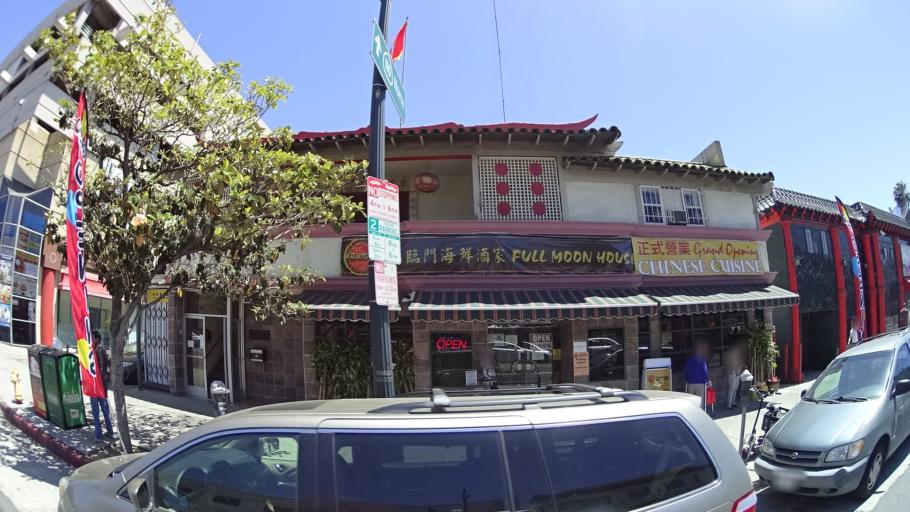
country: US
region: California
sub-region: Los Angeles County
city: Los Angeles
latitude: 34.0660
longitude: -118.2379
